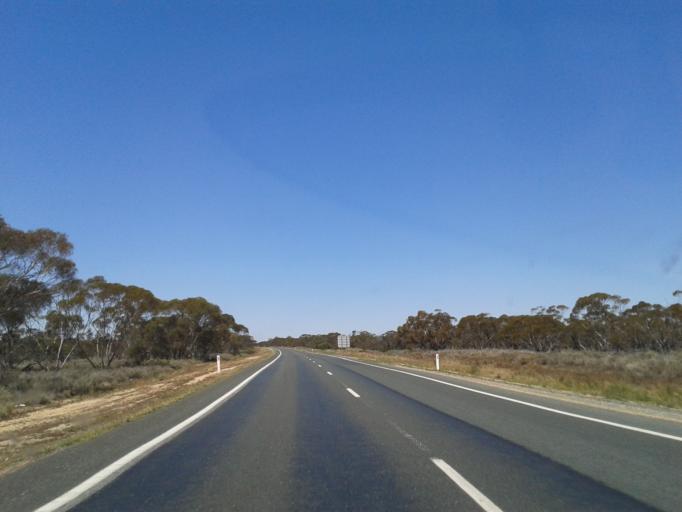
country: AU
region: New South Wales
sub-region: Wentworth
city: Gol Gol
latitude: -34.4285
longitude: 142.4565
